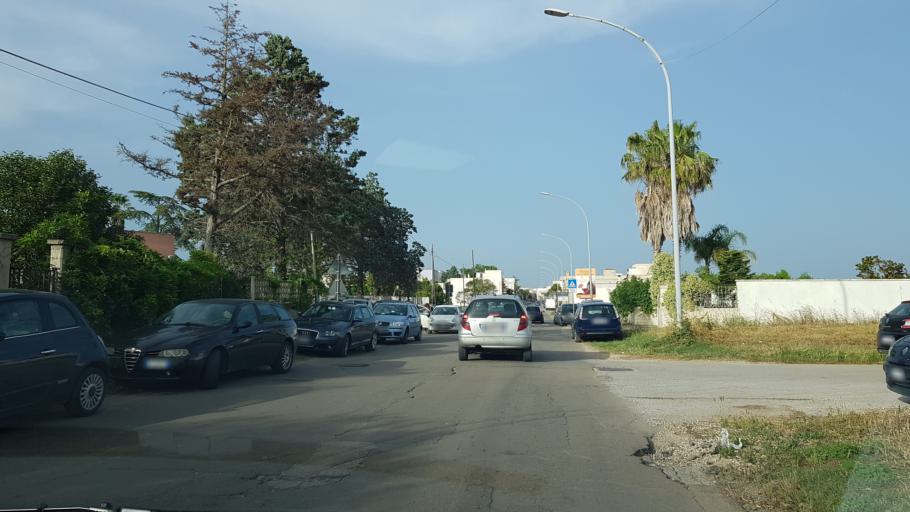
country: IT
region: Apulia
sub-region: Provincia di Brindisi
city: San Donaci
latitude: 40.4442
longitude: 17.9134
